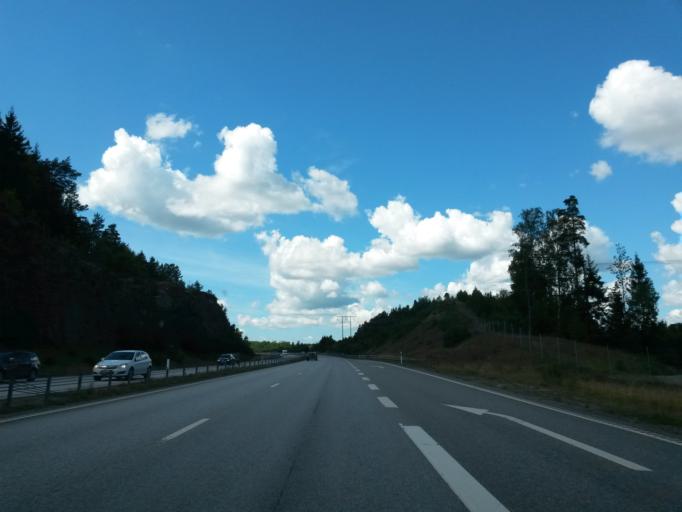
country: SE
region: Vaestra Goetaland
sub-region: Uddevalla Kommun
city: Uddevalla
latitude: 58.3314
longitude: 12.0733
